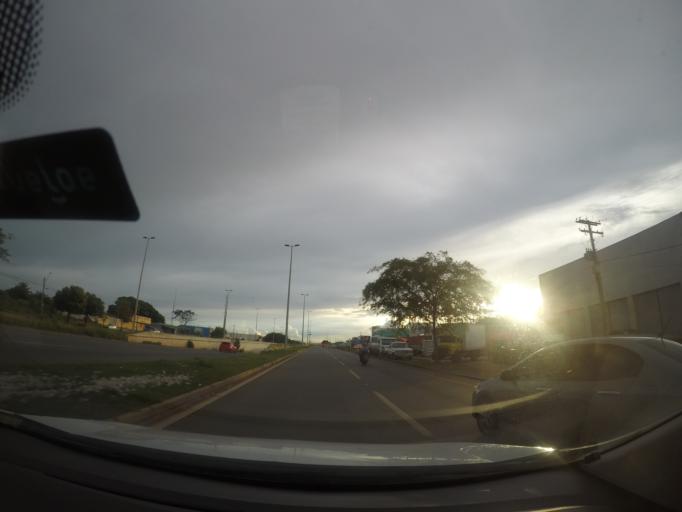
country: BR
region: Goias
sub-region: Goiania
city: Goiania
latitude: -16.7526
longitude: -49.3361
